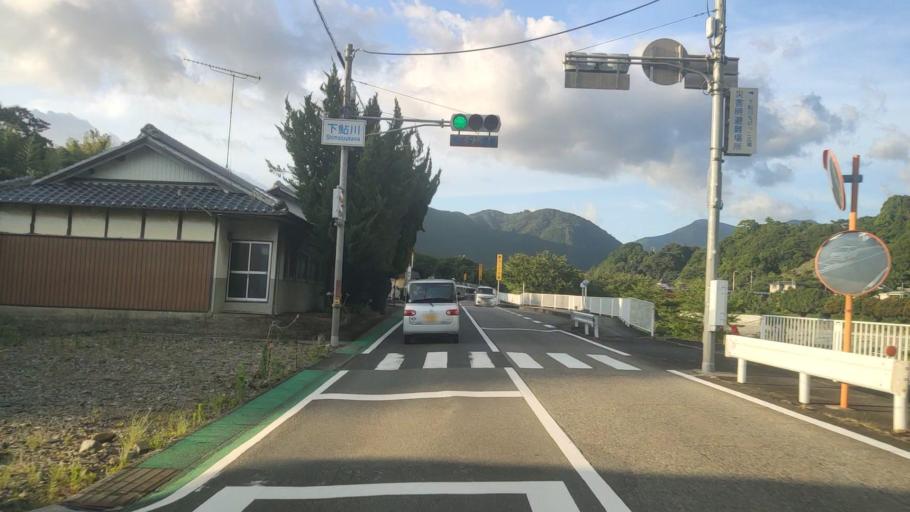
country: JP
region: Wakayama
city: Tanabe
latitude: 33.7202
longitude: 135.4813
